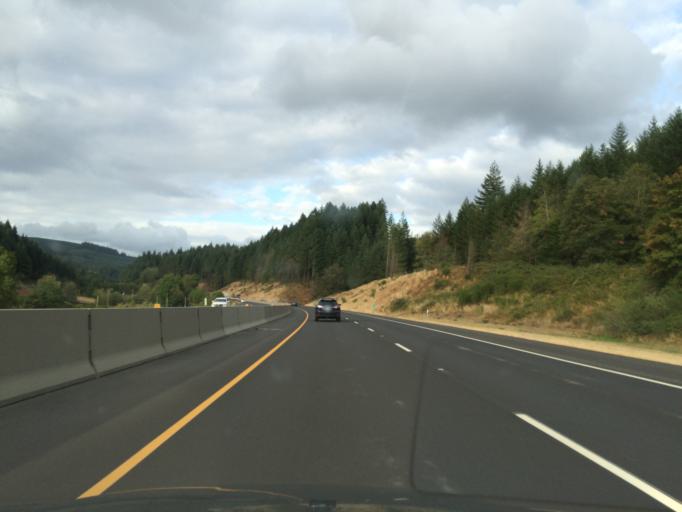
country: US
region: Oregon
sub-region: Lane County
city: Cottage Grove
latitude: 43.7372
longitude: -123.1890
